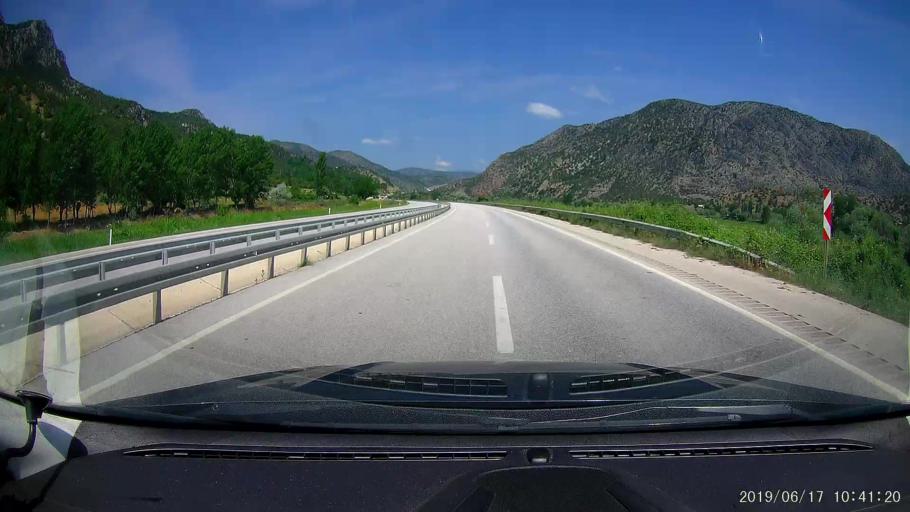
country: TR
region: Corum
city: Kargi
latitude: 41.0385
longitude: 34.5790
